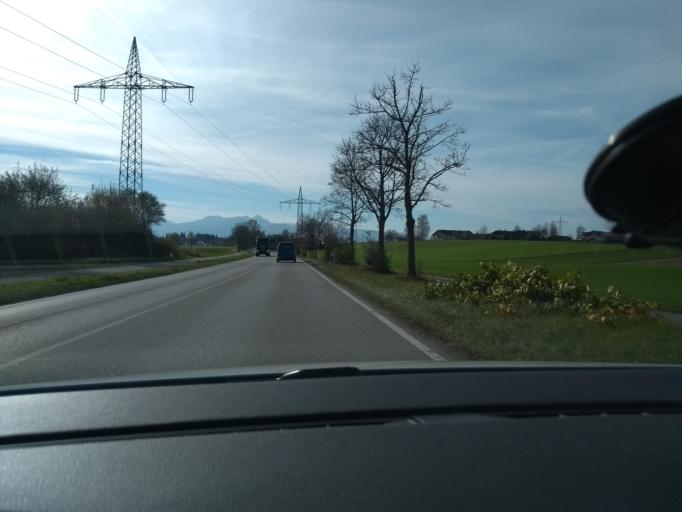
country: DE
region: Bavaria
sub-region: Upper Bavaria
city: Stephanskirchen
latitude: 47.8774
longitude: 12.1776
